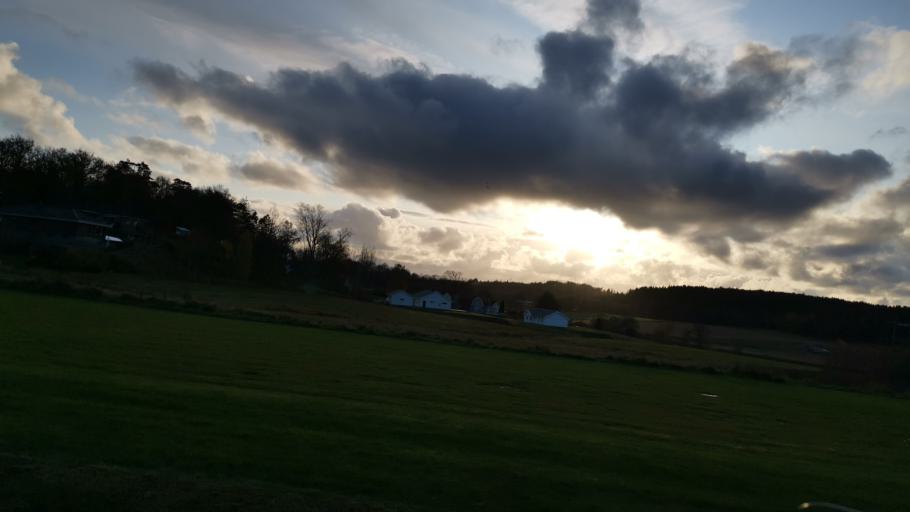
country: SE
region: Vaestra Goetaland
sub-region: Munkedals Kommun
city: Munkedal
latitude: 58.4653
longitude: 11.6626
